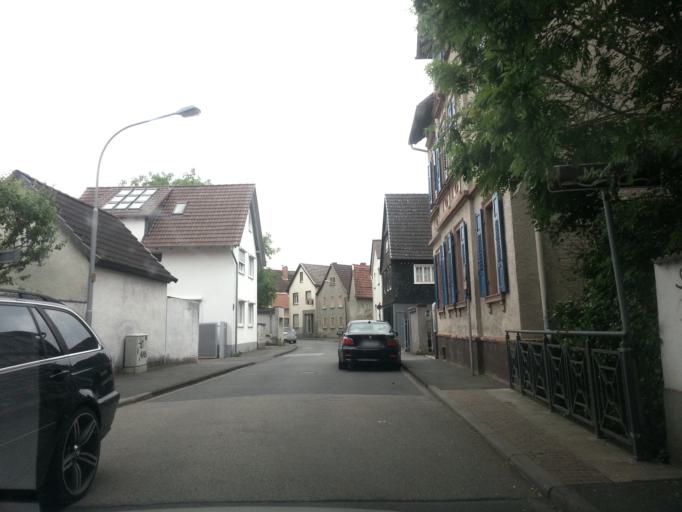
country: DE
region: Hesse
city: Pfungstadt
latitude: 49.7999
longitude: 8.5972
